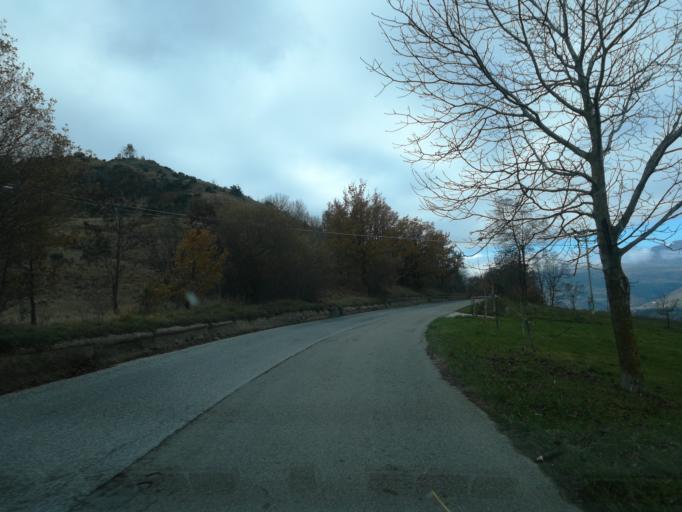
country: IT
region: Molise
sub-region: Provincia di Isernia
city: Agnone
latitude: 41.8249
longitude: 14.3805
